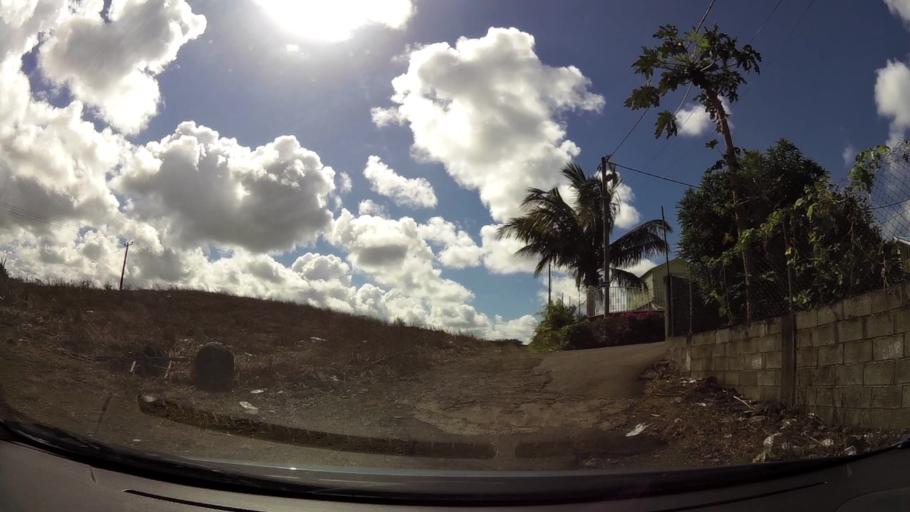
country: MU
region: Grand Port
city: Plaine Magnien
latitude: -20.4272
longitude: 57.6567
